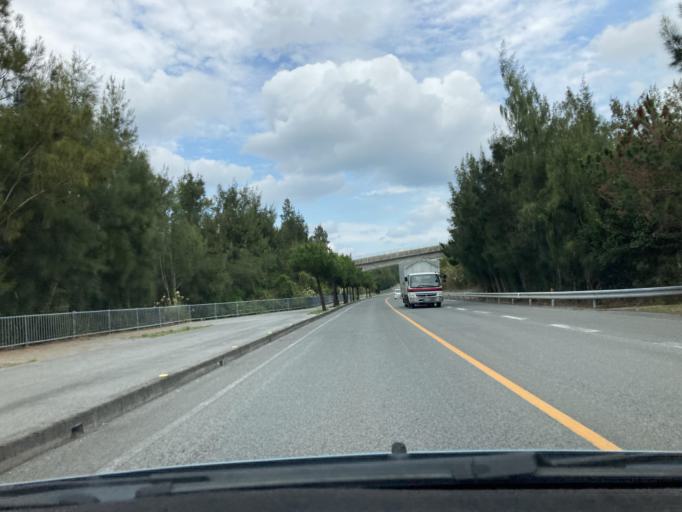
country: JP
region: Okinawa
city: Ishikawa
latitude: 26.4560
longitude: 127.8222
